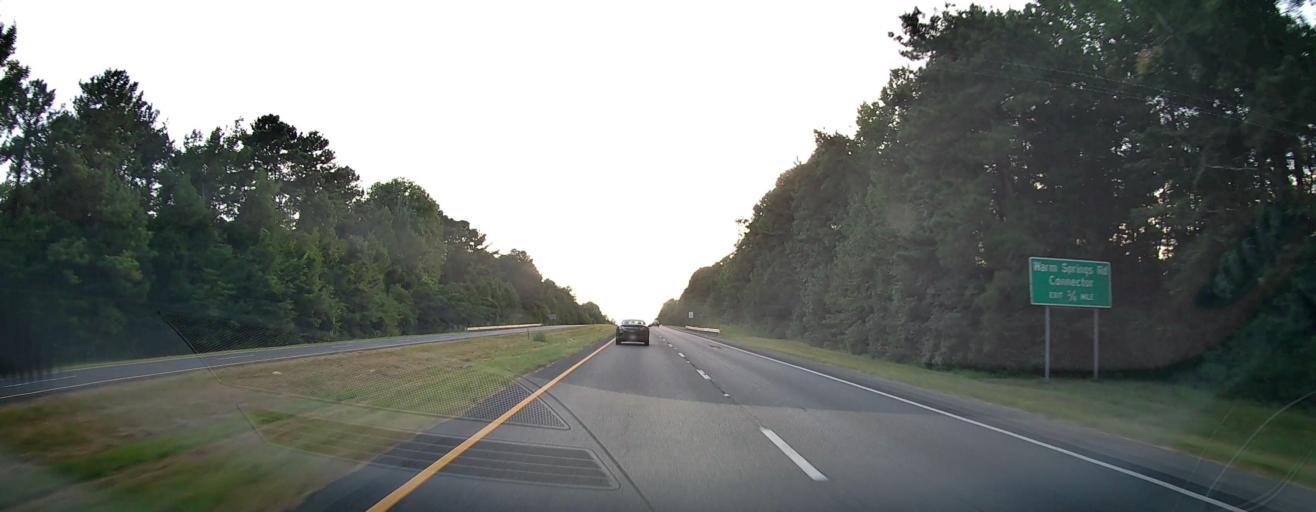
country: US
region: Georgia
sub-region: Muscogee County
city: Columbus
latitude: 32.5208
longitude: -84.9006
